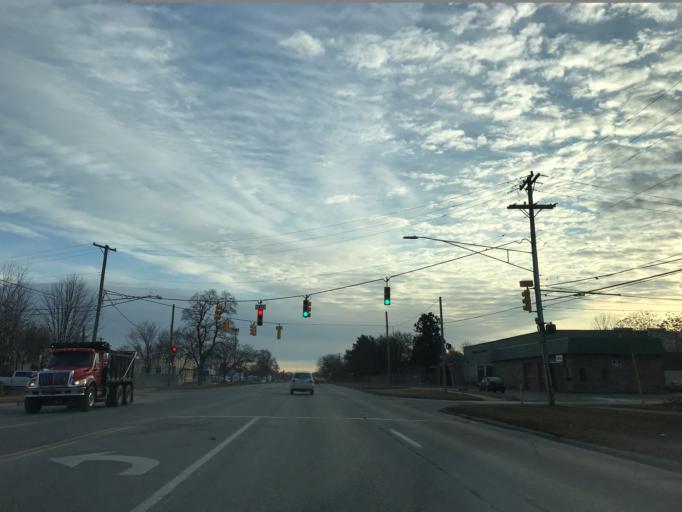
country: US
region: Michigan
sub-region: Oakland County
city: Farmington
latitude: 42.4413
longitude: -83.3470
